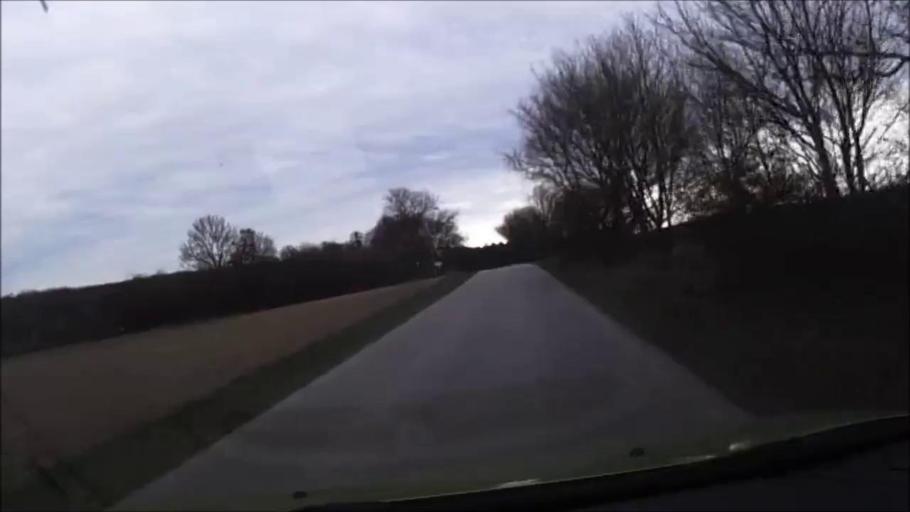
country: AT
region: Burgenland
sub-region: Eisenstadt-Umgebung
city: Loretto
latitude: 47.9084
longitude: 16.5150
